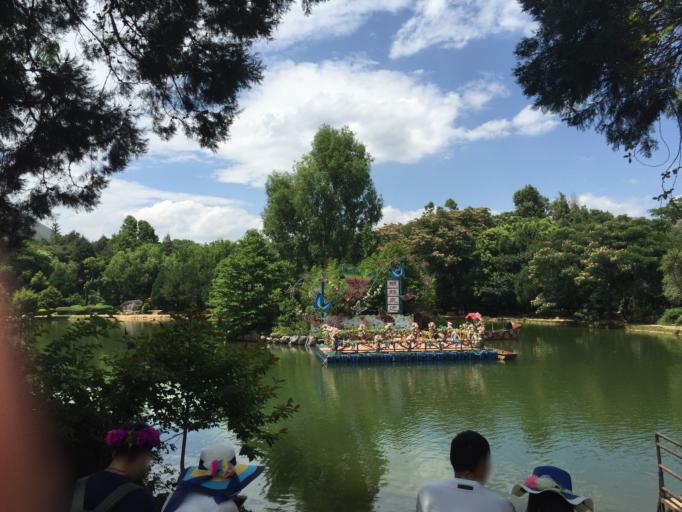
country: CN
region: Yunnan
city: Yuhu
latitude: 25.9080
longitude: 100.0962
